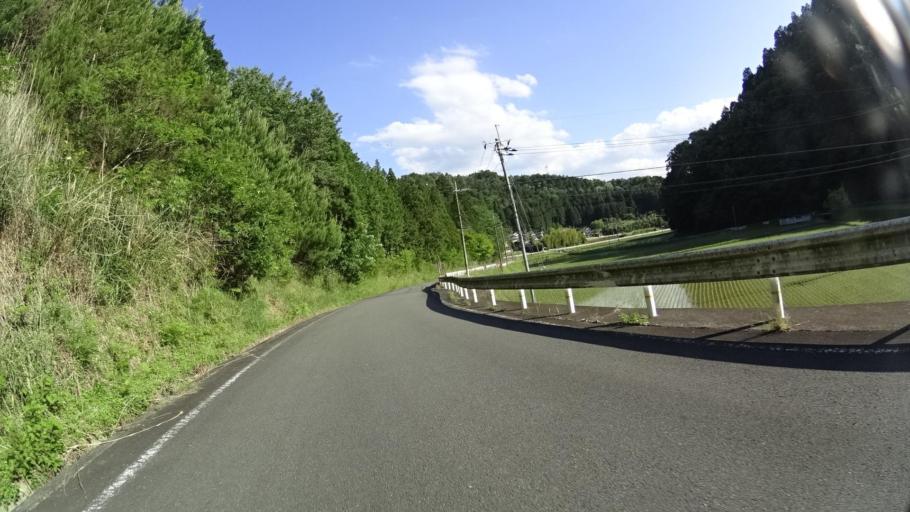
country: JP
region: Kyoto
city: Kameoka
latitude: 34.9682
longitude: 135.5627
